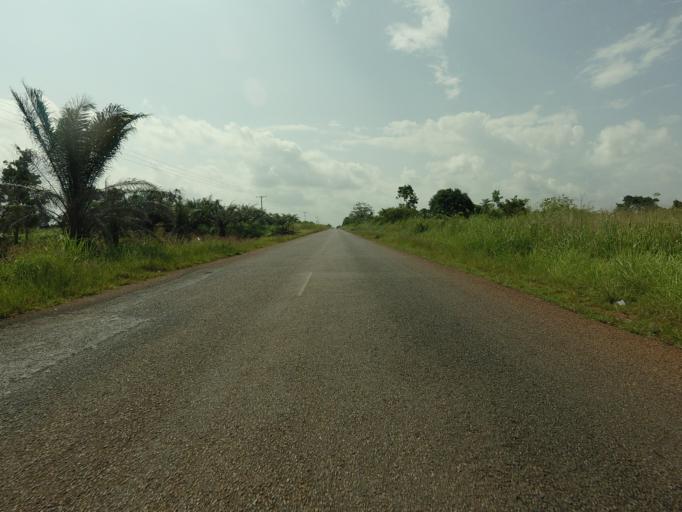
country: TG
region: Maritime
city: Tsevie
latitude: 6.3450
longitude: 0.8726
